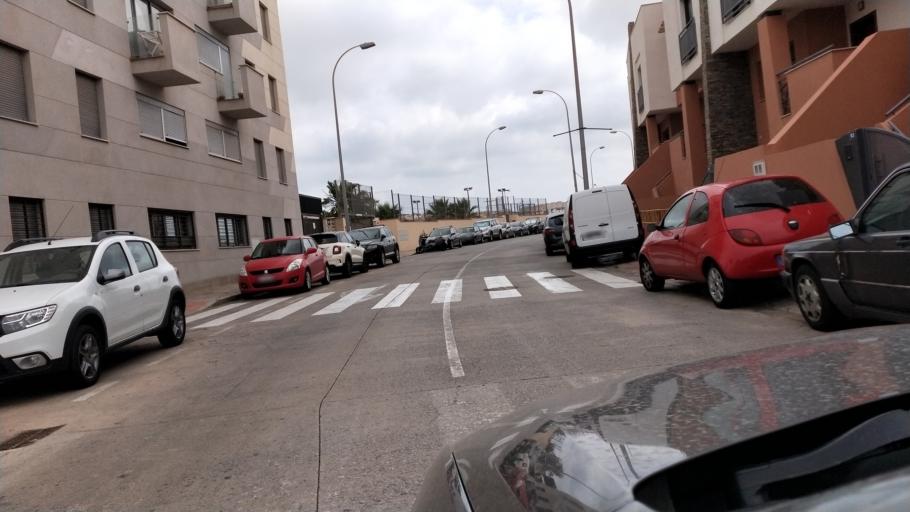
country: ES
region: Melilla
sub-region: Melilla
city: Melilla
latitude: 35.2898
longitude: -2.9567
